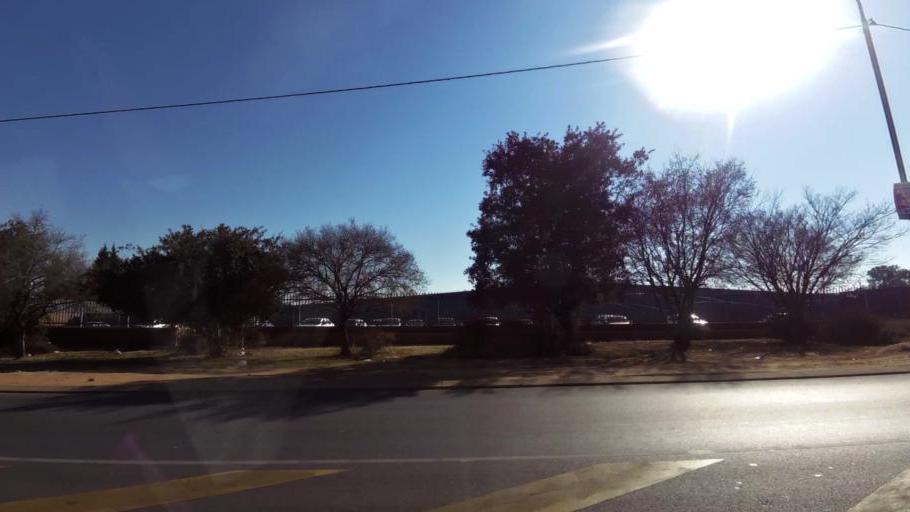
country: ZA
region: Gauteng
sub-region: City of Johannesburg Metropolitan Municipality
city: Johannesburg
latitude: -26.2394
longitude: 28.0016
